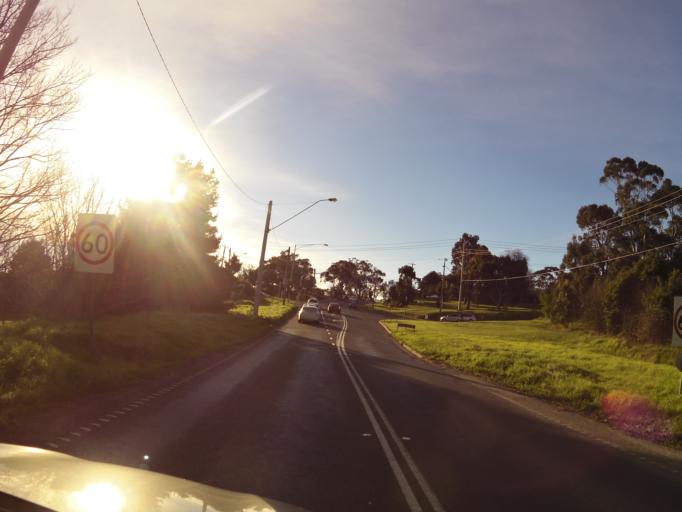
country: AU
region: Victoria
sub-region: Knox
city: Ferntree Gully
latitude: -37.9012
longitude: 145.2949
